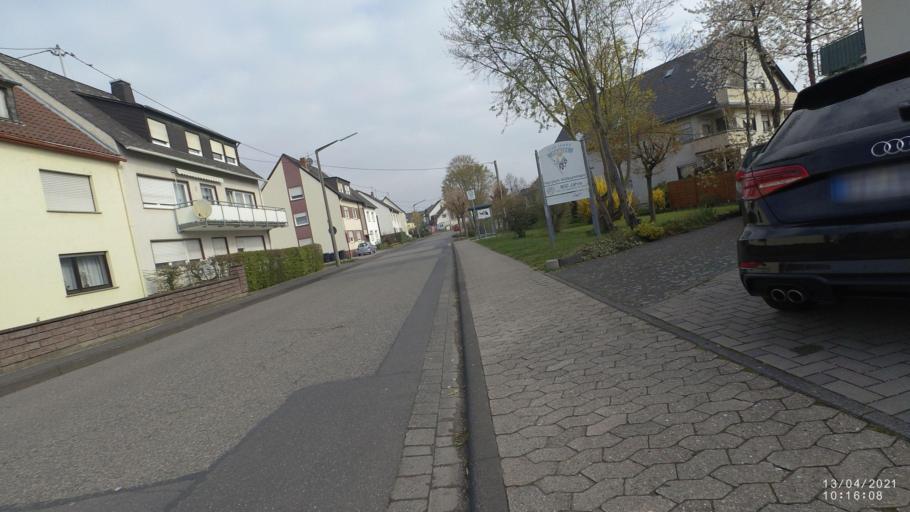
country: DE
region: Rheinland-Pfalz
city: Urmitz
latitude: 50.4110
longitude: 7.5122
